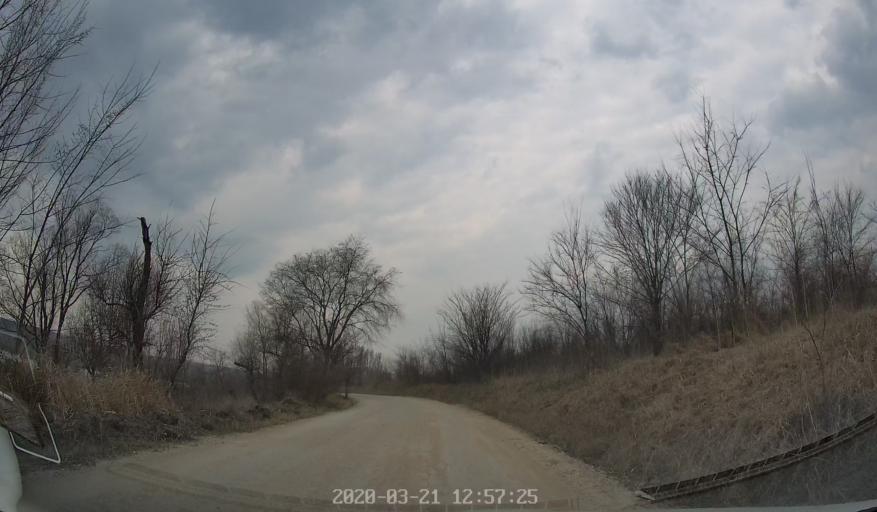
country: MD
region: Laloveni
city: Ialoveni
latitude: 46.9594
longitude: 28.7433
